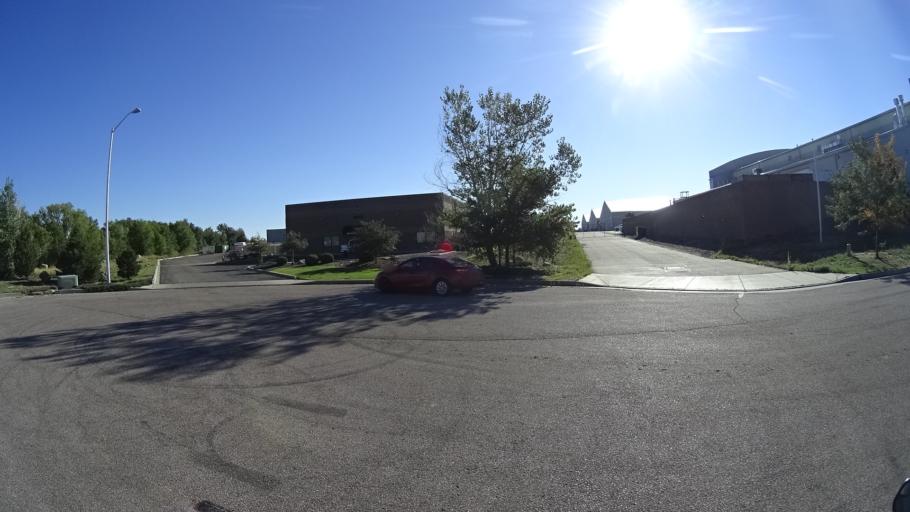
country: US
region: Colorado
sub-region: El Paso County
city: Cimarron Hills
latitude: 38.8218
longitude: -104.7229
